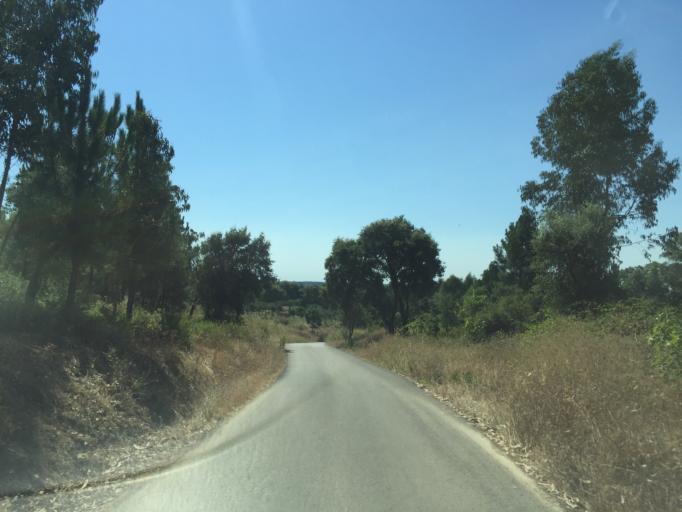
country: PT
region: Santarem
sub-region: Ferreira do Zezere
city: Ferreira do Zezere
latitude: 39.5935
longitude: -8.2879
